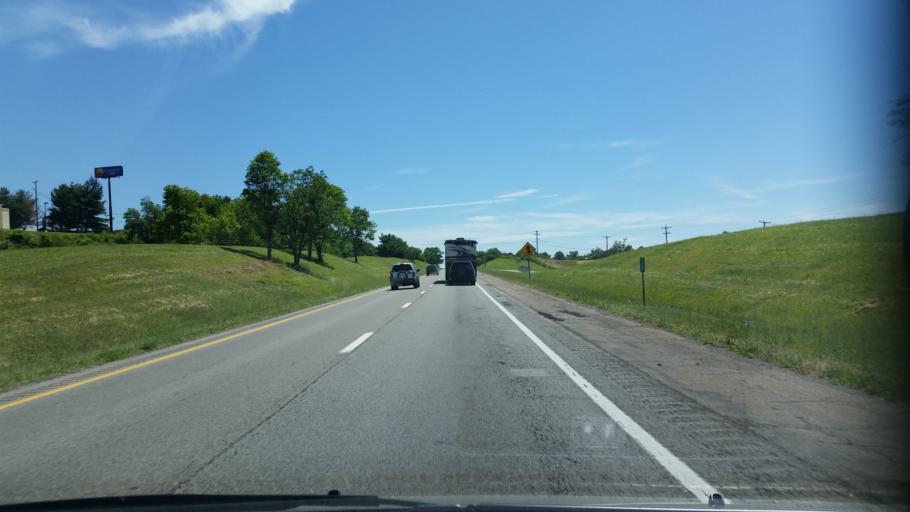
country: US
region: Virginia
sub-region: Wythe County
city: Wytheville
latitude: 36.9603
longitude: -81.0978
